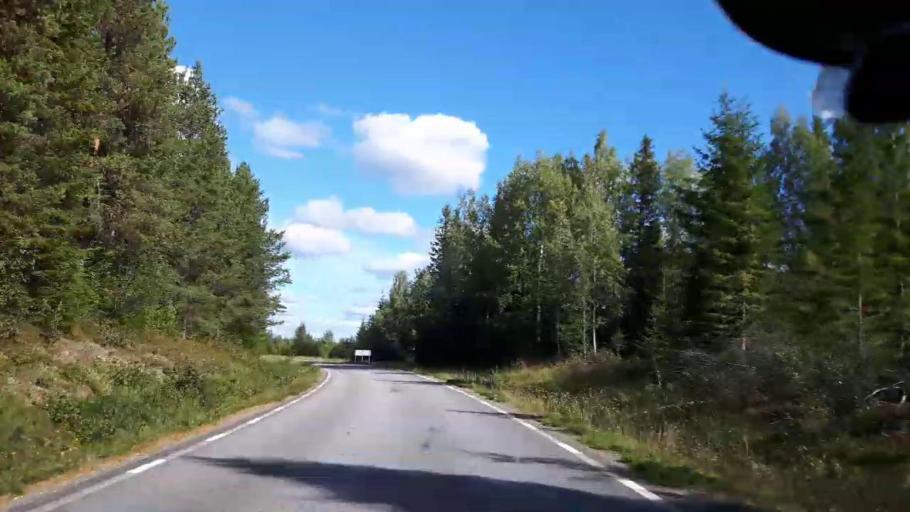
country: SE
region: Jaemtland
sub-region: OEstersunds Kommun
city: Brunflo
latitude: 63.2072
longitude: 15.2468
